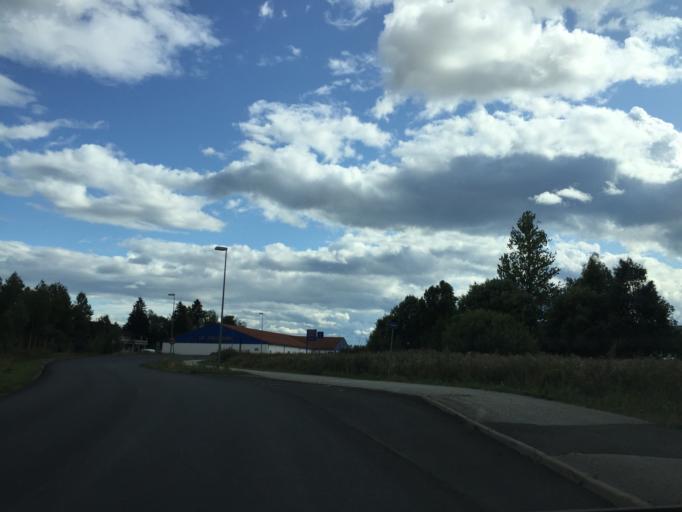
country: NO
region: Ostfold
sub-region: Askim
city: Askim
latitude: 59.5865
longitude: 11.1342
